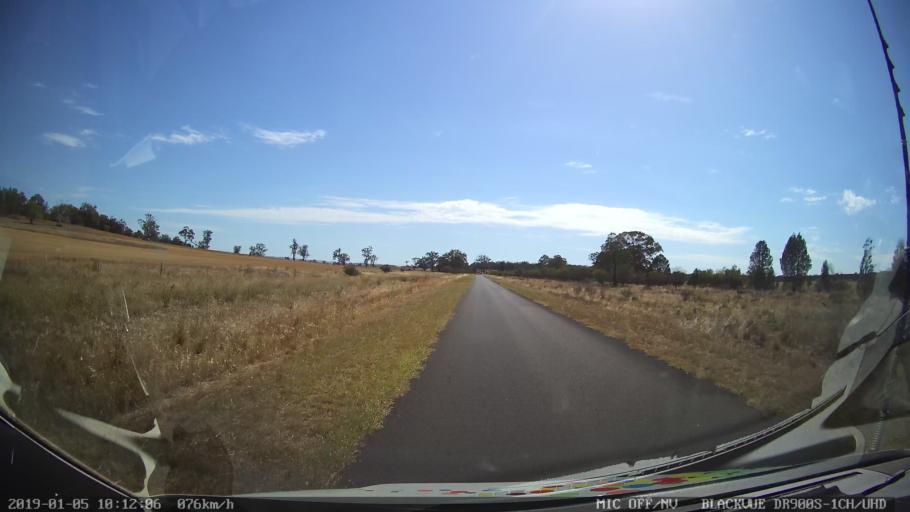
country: AU
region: New South Wales
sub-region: Gilgandra
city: Gilgandra
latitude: -31.6097
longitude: 148.9091
